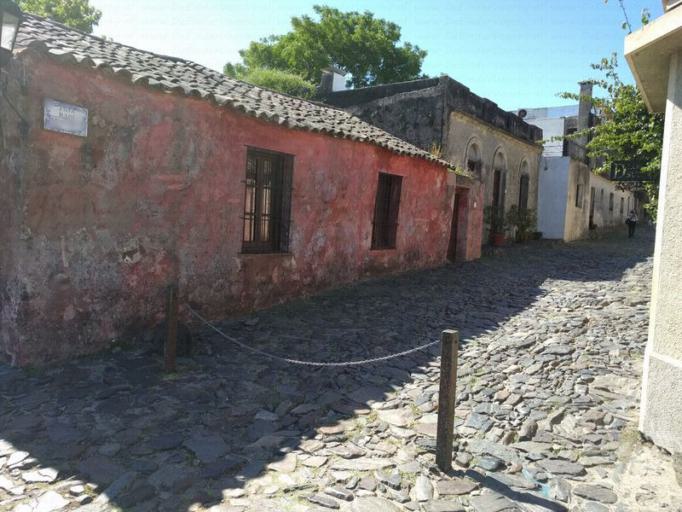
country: UY
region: Colonia
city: Colonia del Sacramento
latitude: -34.4731
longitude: -57.8511
